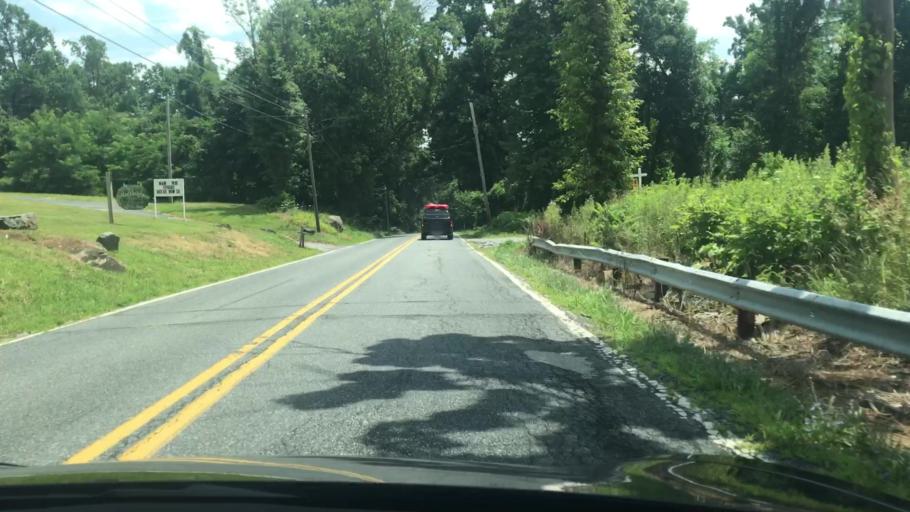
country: US
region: Pennsylvania
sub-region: York County
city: Valley Green
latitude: 40.1284
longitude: -76.7890
